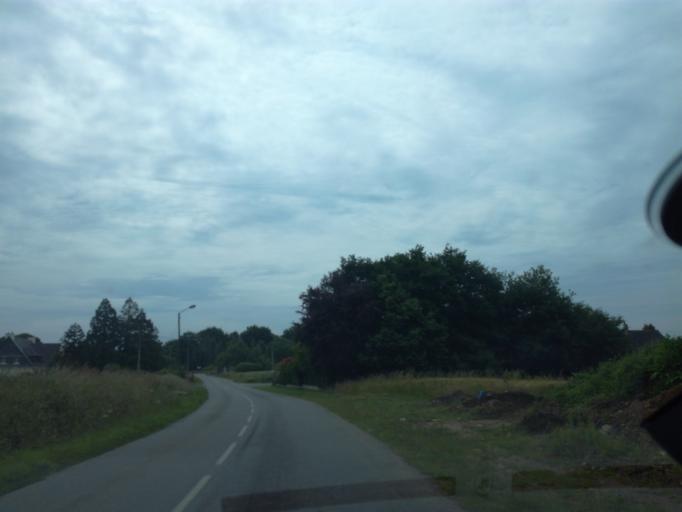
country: FR
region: Brittany
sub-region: Departement du Morbihan
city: Saint-Thuriau
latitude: 48.0247
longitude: -2.9625
